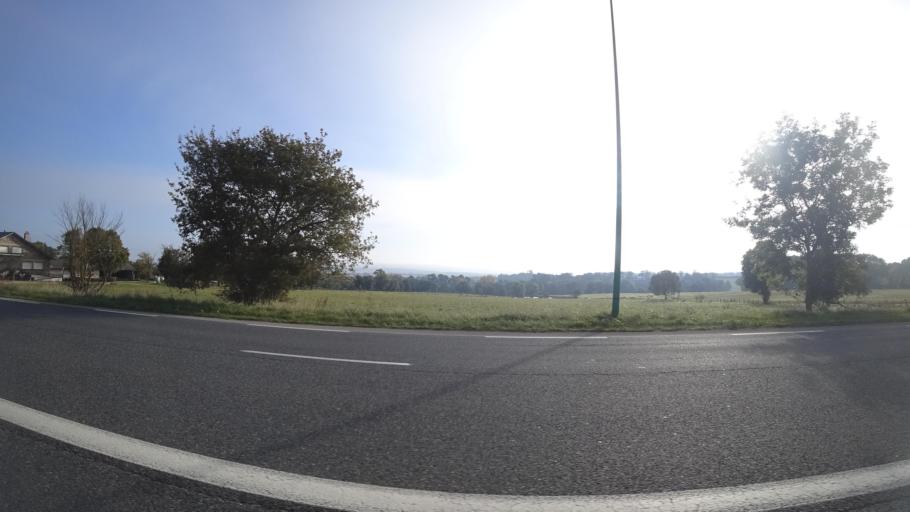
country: FR
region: Midi-Pyrenees
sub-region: Departement de l'Aveyron
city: Luc-la-Primaube
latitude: 44.3088
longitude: 2.5574
